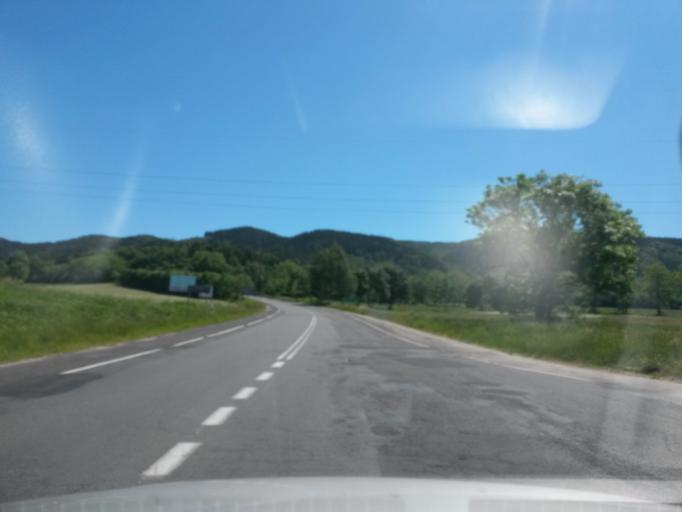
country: PL
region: Lower Silesian Voivodeship
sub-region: Powiat jeleniogorski
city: Kowary
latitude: 50.7915
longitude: 15.8530
